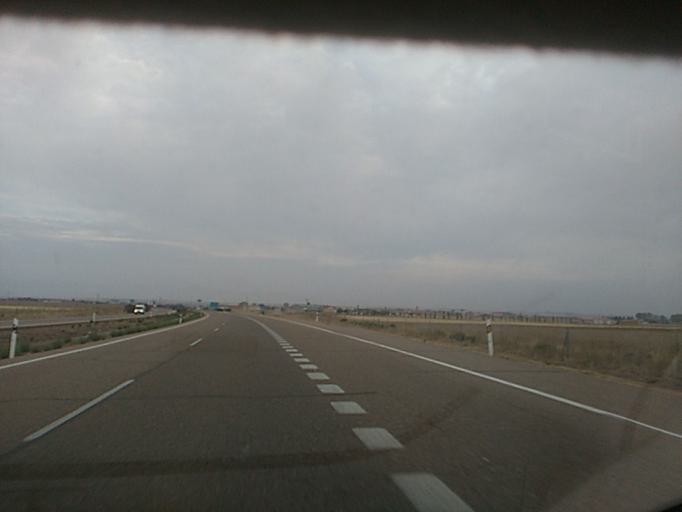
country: ES
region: Castille and Leon
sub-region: Provincia de Zamora
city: Villalpando
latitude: 41.8492
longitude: -5.4021
